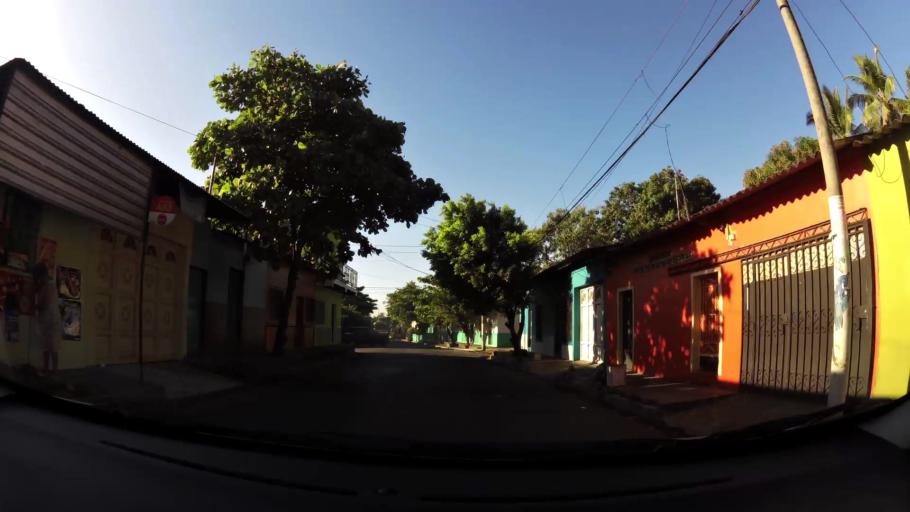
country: SV
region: Sonsonate
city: San Antonio del Monte
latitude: 13.7165
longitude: -89.7333
